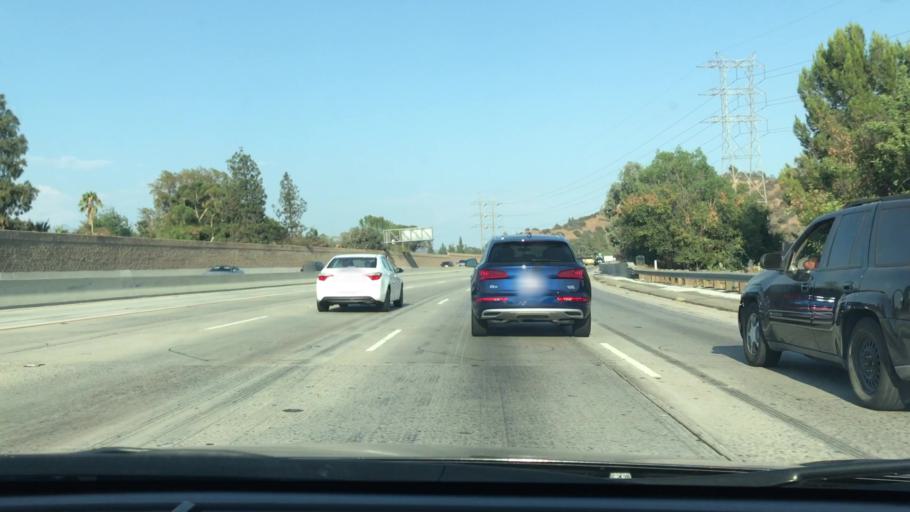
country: US
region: California
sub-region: Los Angeles County
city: Burbank
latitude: 34.1550
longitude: -118.3185
